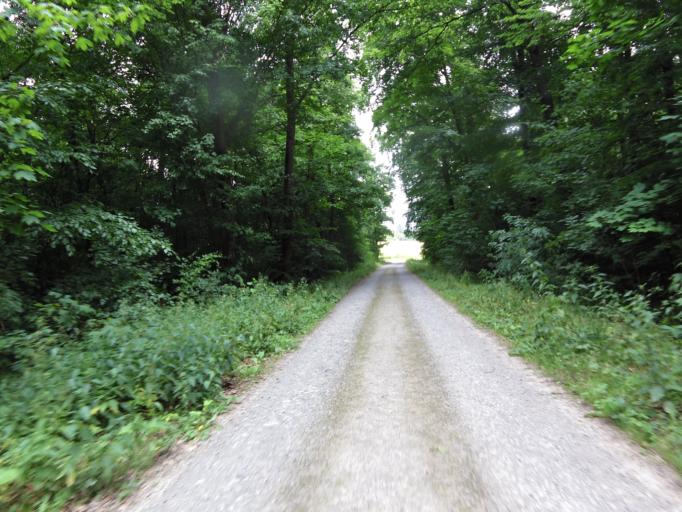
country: DE
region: Bavaria
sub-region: Regierungsbezirk Unterfranken
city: Reichenberg
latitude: 49.7587
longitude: 9.9144
